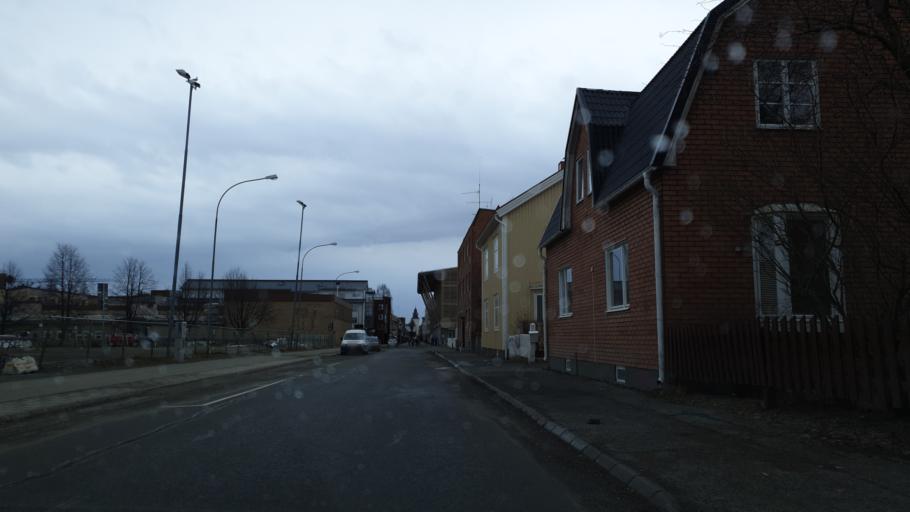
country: SE
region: Vaesterbotten
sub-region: Skelleftea Kommun
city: Skelleftea
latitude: 64.7513
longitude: 20.9428
